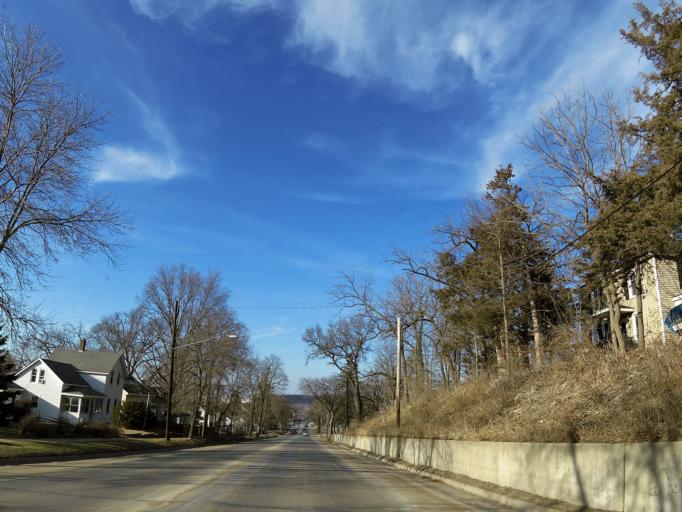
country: US
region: Minnesota
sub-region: Goodhue County
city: Cannon Falls
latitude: 44.5021
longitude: -92.9058
